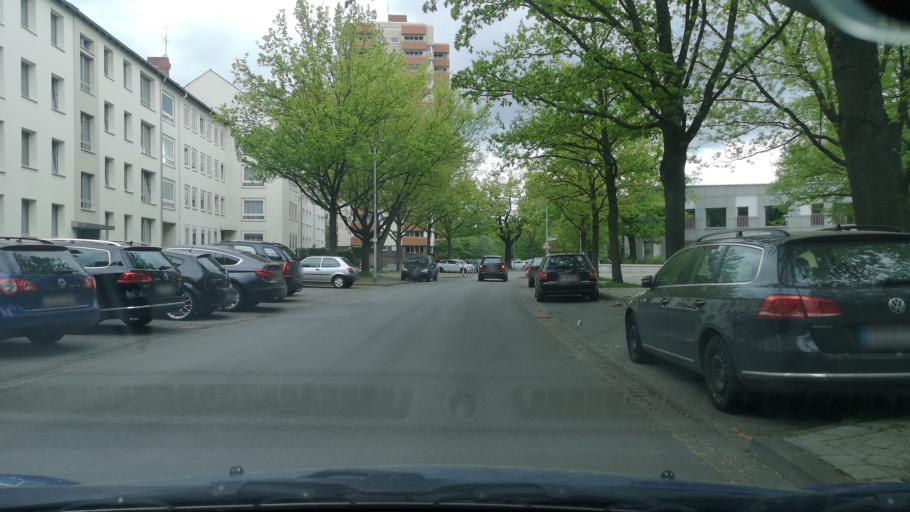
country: DE
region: Lower Saxony
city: Hannover
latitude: 52.3999
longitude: 9.7159
